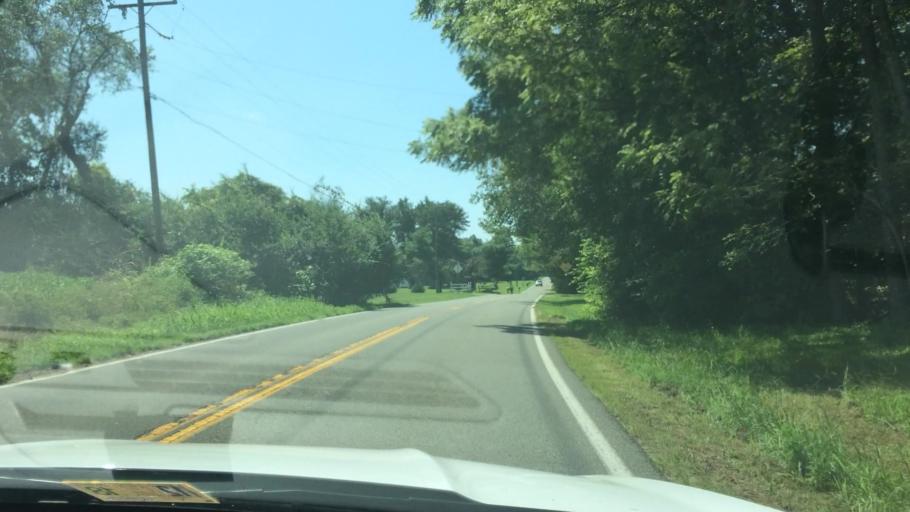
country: US
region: Virginia
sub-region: Charles City County
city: Charles City
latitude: 37.3959
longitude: -77.0492
